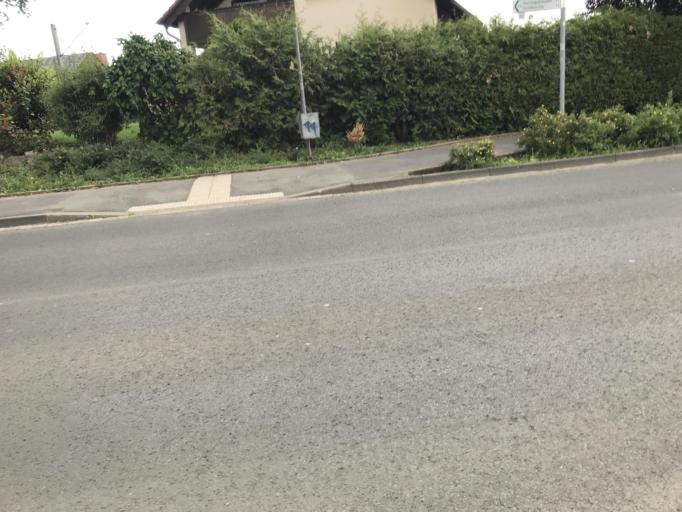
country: DE
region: Hesse
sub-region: Regierungsbezirk Kassel
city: Baunatal
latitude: 51.2526
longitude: 9.4024
